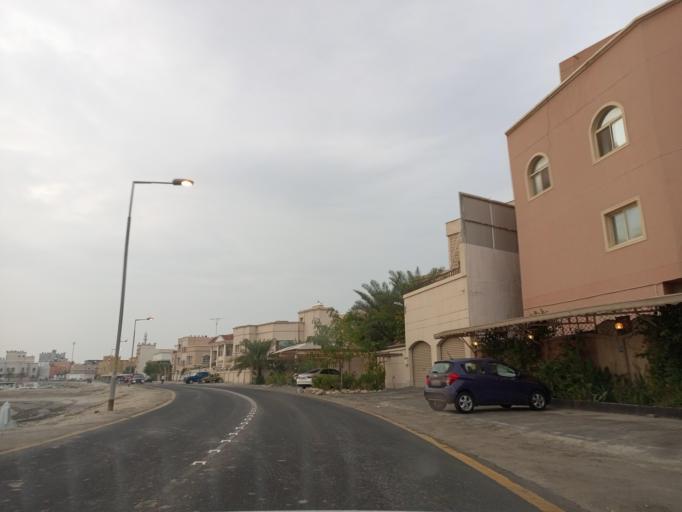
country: BH
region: Muharraq
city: Al Hadd
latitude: 26.2450
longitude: 50.6476
